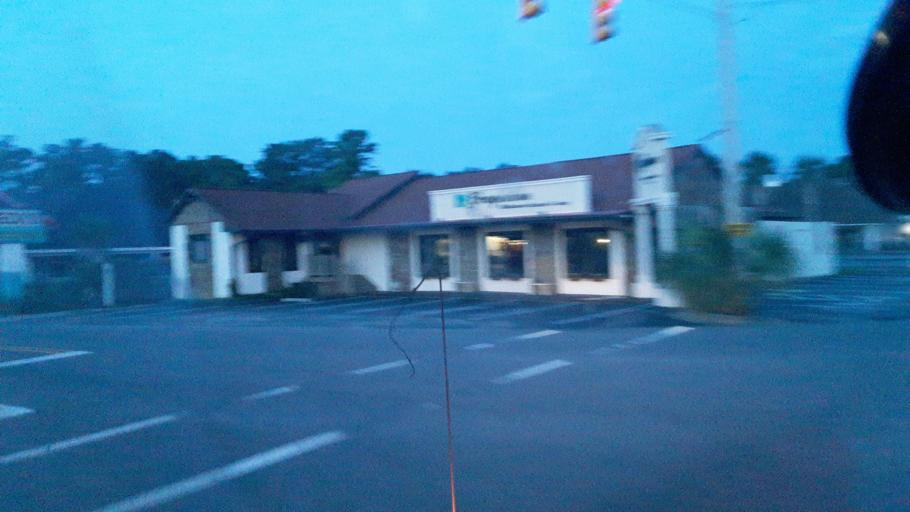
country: US
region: North Carolina
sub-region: Brunswick County
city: Calabash
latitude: 33.8908
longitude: -78.5682
